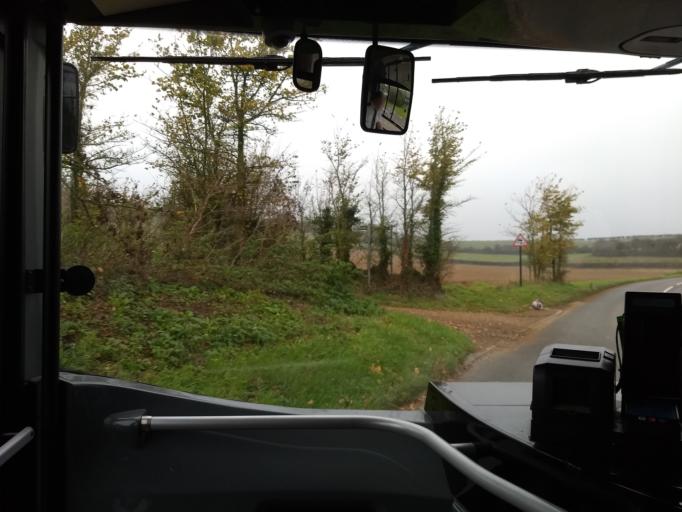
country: GB
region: England
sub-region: Isle of Wight
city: Newchurch
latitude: 50.6771
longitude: -1.2504
